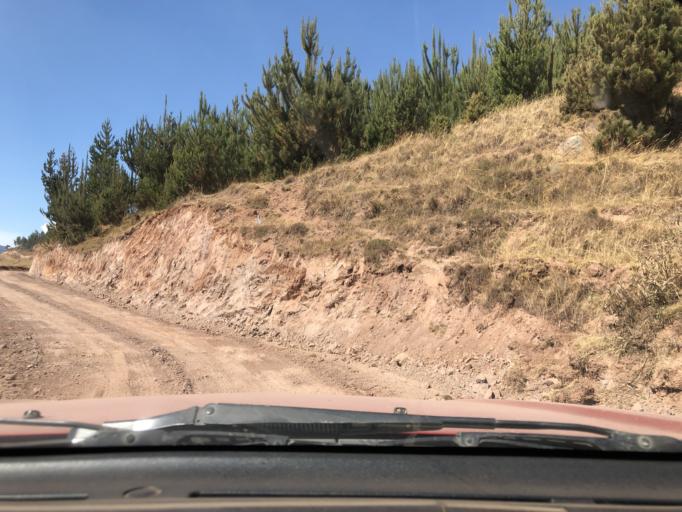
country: PE
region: Ayacucho
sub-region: Provincia de La Mar
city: Chilcas
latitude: -13.1824
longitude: -73.8442
